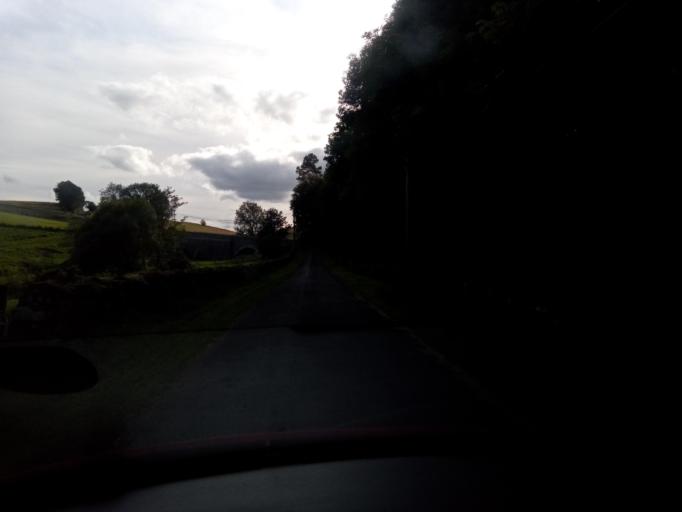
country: GB
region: Scotland
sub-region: The Scottish Borders
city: Kelso
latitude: 55.4796
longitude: -2.3535
